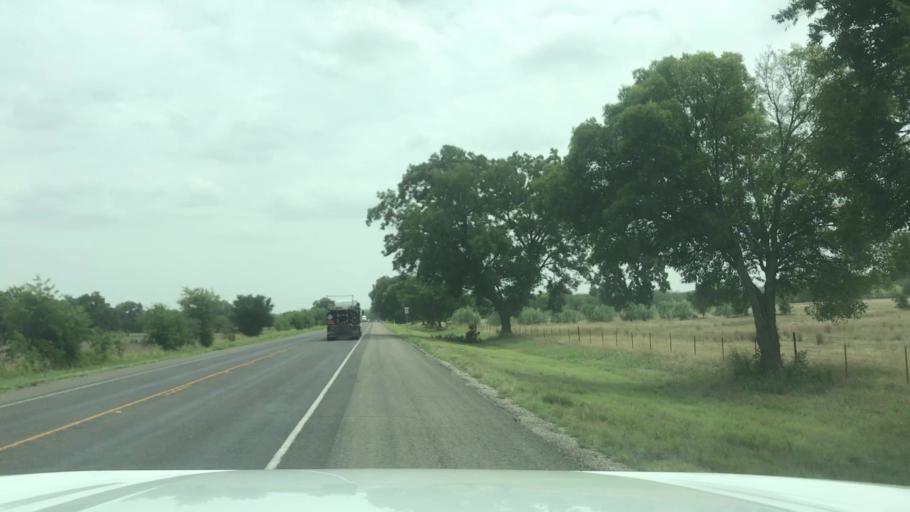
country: US
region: Texas
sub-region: Bosque County
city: Valley Mills
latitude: 31.6727
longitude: -97.5063
